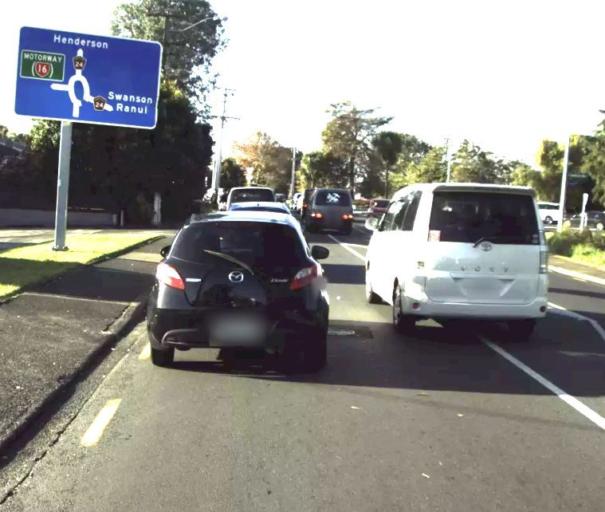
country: NZ
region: Auckland
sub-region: Auckland
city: Rosebank
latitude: -36.8600
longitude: 174.6111
